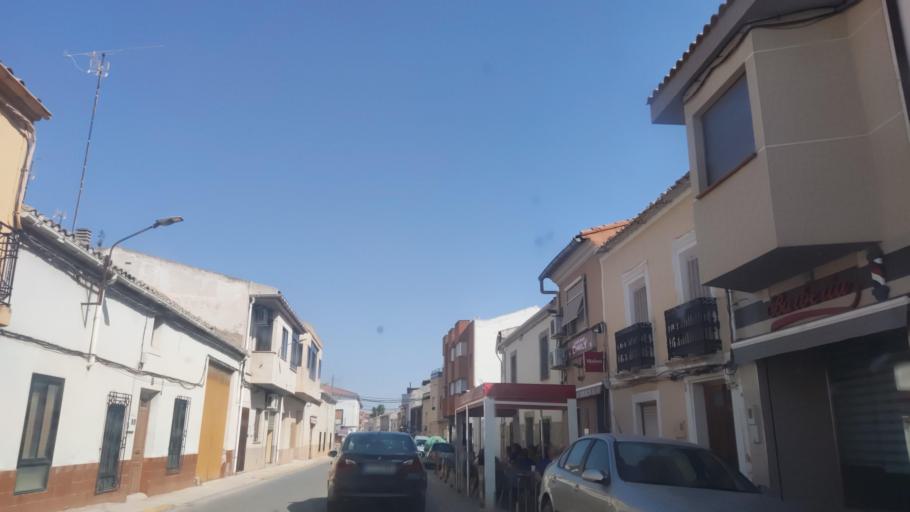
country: ES
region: Castille-La Mancha
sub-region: Provincia de Albacete
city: La Gineta
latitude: 39.1131
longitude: -1.9961
